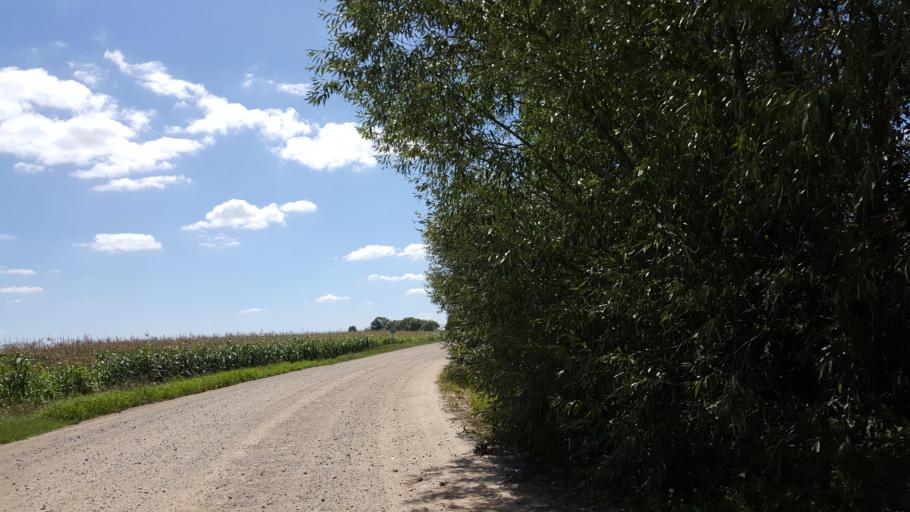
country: BY
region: Brest
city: Horad Kobryn
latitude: 52.3309
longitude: 24.3741
